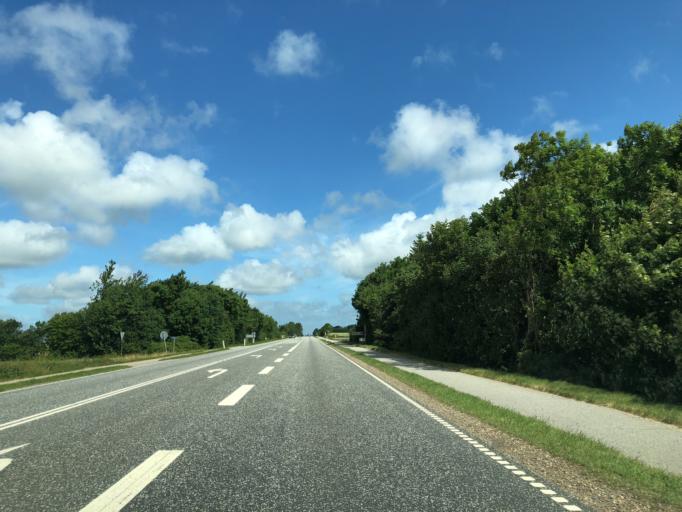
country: DK
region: Central Jutland
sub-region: Struer Kommune
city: Struer
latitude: 56.4340
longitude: 8.5970
